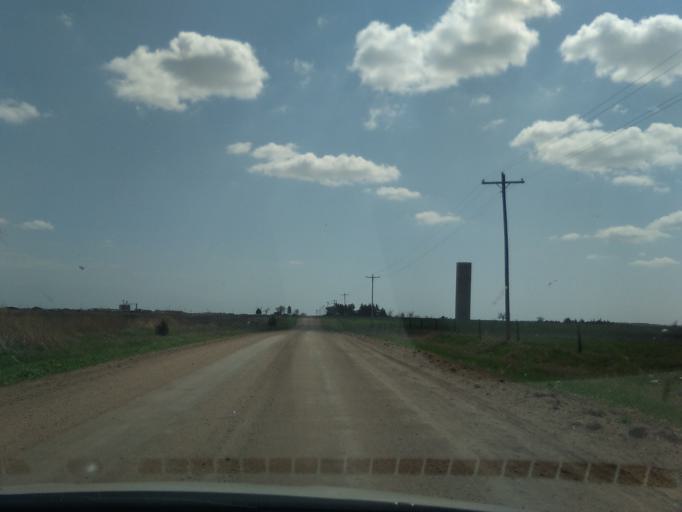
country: US
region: Nebraska
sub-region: Thayer County
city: Hebron
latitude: 40.3412
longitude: -97.4387
